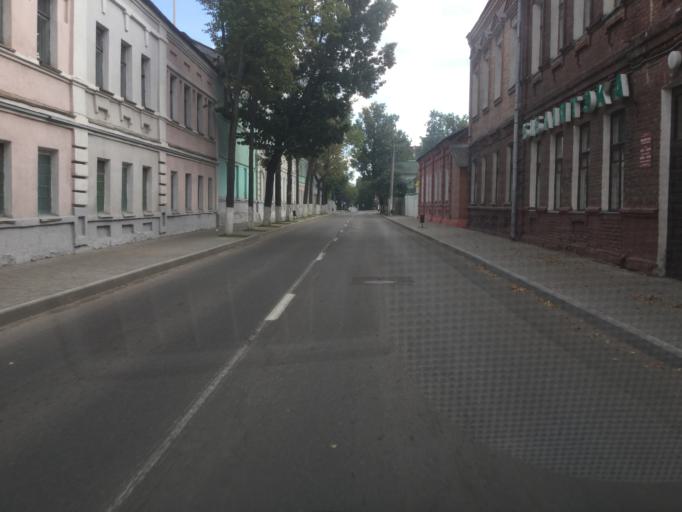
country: BY
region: Vitebsk
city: Vitebsk
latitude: 55.1986
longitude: 30.1909
